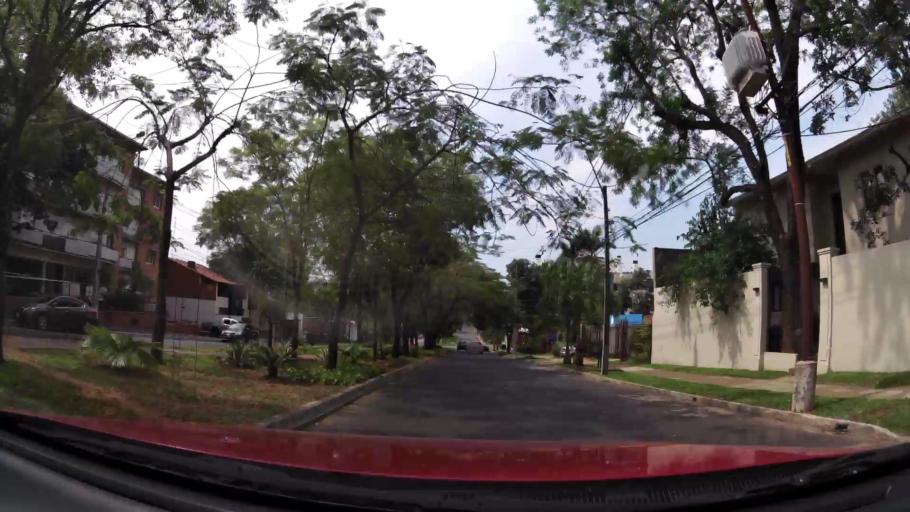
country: PY
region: Asuncion
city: Asuncion
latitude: -25.2819
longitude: -57.5799
